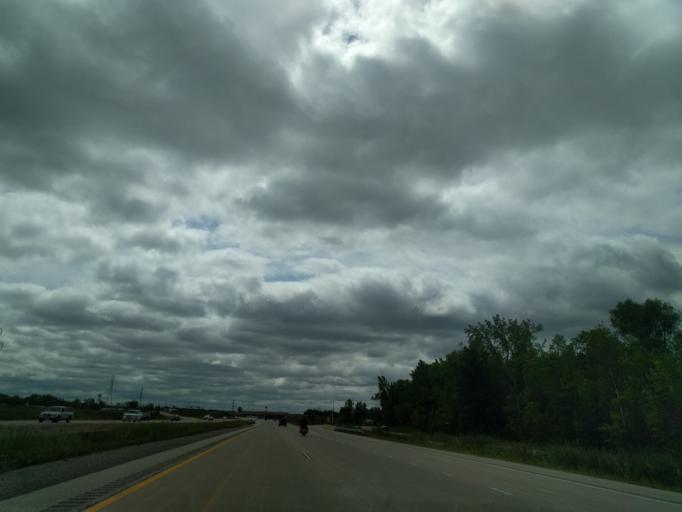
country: US
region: Wisconsin
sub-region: Brown County
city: Suamico
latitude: 44.5969
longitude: -88.0496
